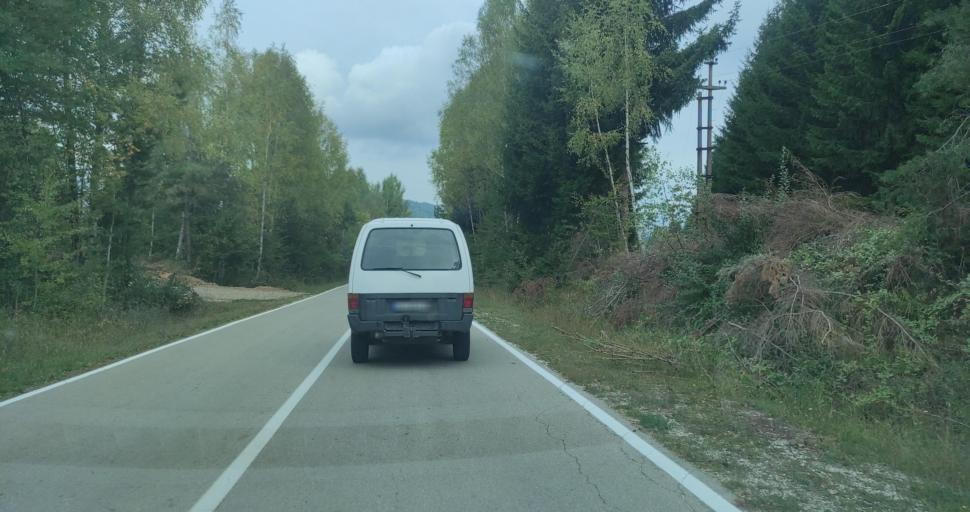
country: RS
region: Central Serbia
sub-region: Jablanicki Okrug
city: Crna Trava
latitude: 42.6827
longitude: 22.3141
